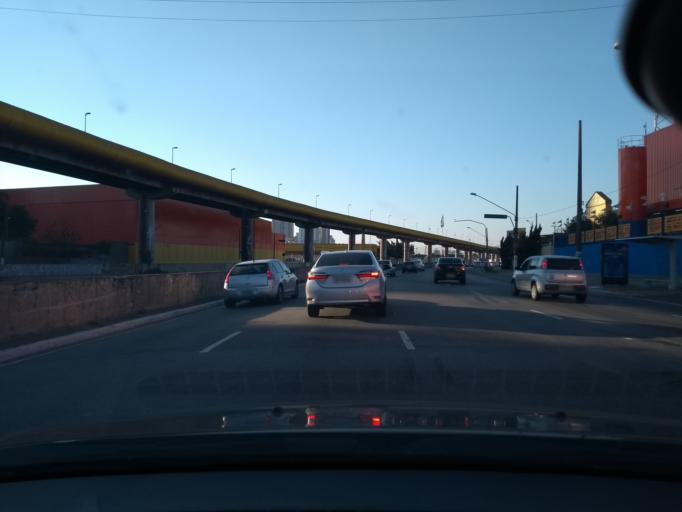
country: BR
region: Sao Paulo
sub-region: Sao Paulo
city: Sao Paulo
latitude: -23.5846
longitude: -46.5993
